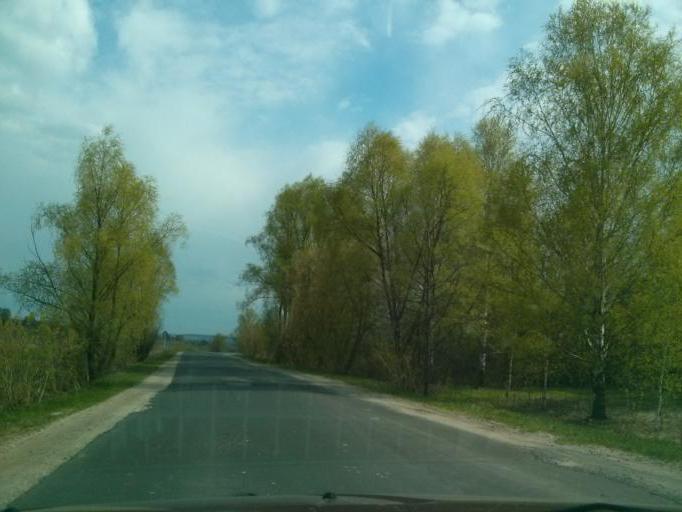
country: RU
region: Nizjnij Novgorod
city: Shimorskoye
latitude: 55.3712
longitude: 41.9271
